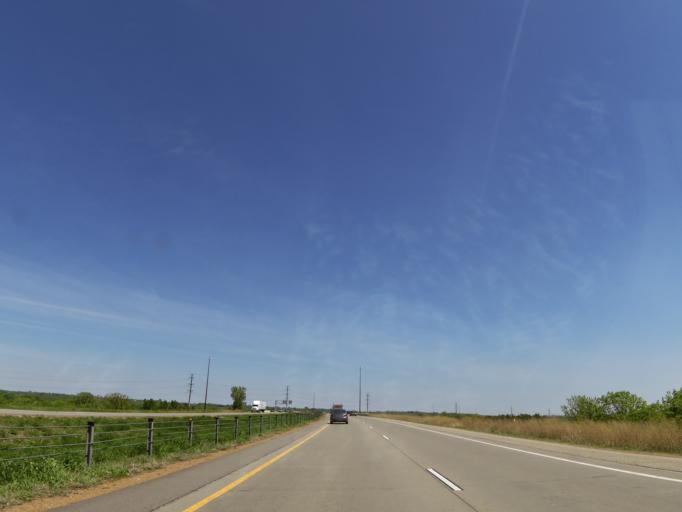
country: US
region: Minnesota
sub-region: Scott County
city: Prior Lake
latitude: 44.7848
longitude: -93.4167
